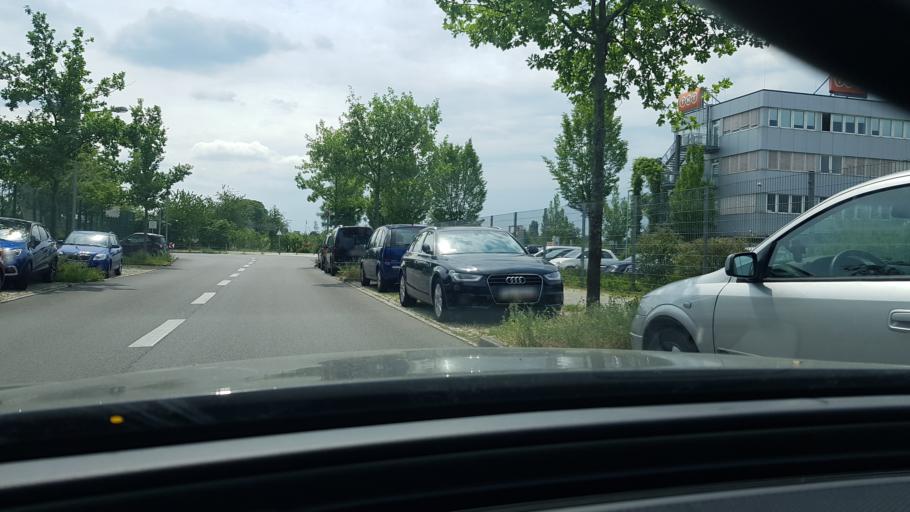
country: DE
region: Berlin
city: Charlottenburg-Nord
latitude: 52.5446
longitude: 13.3089
